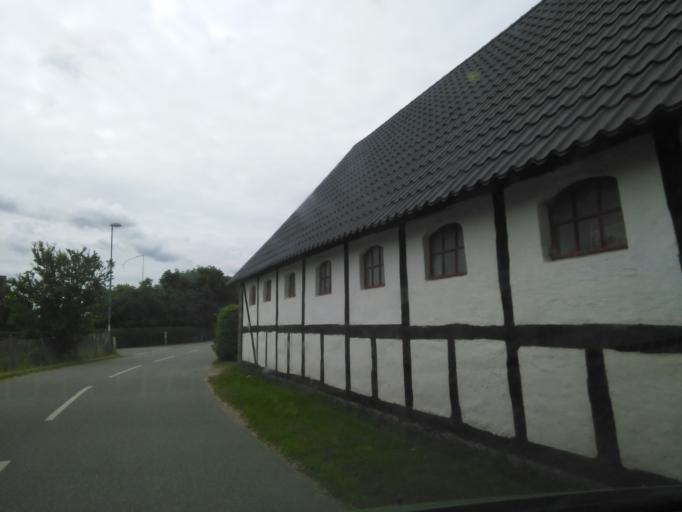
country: DK
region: Central Jutland
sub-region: Arhus Kommune
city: Solbjerg
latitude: 56.0204
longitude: 10.0741
